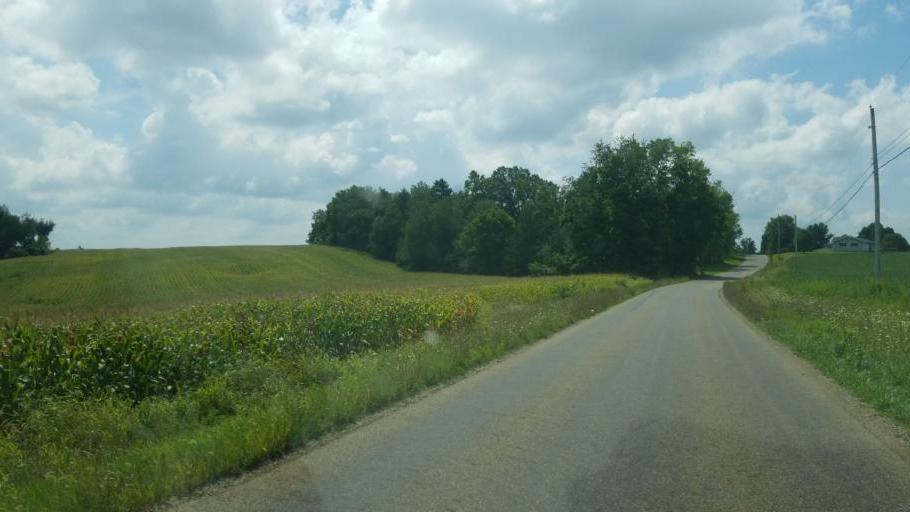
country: US
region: Ohio
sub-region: Knox County
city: Mount Vernon
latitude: 40.4215
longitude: -82.4812
